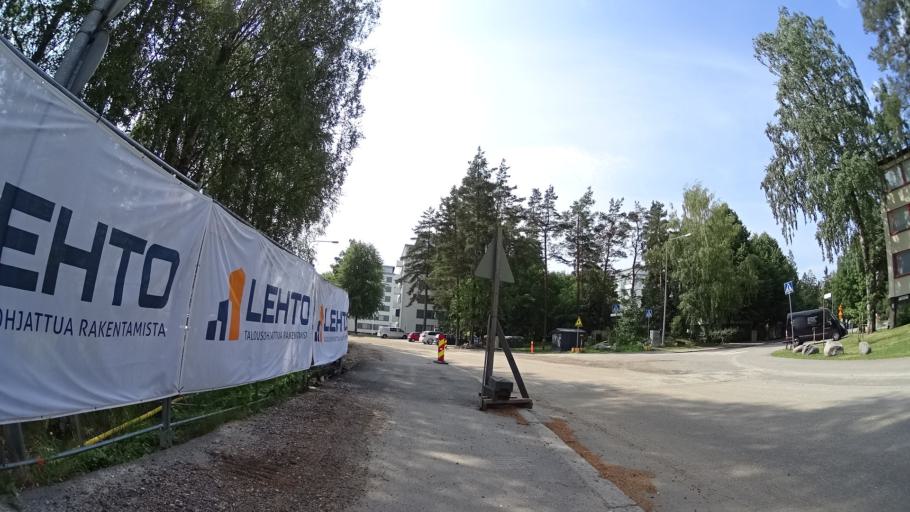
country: FI
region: Uusimaa
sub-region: Helsinki
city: Teekkarikylae
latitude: 60.2667
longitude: 24.8719
